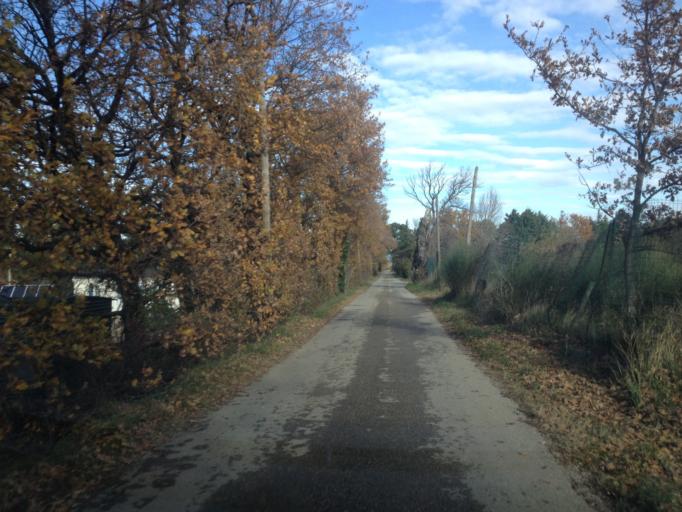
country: FR
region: Provence-Alpes-Cote d'Azur
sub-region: Departement du Vaucluse
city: Jonquieres
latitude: 44.0886
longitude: 4.9195
